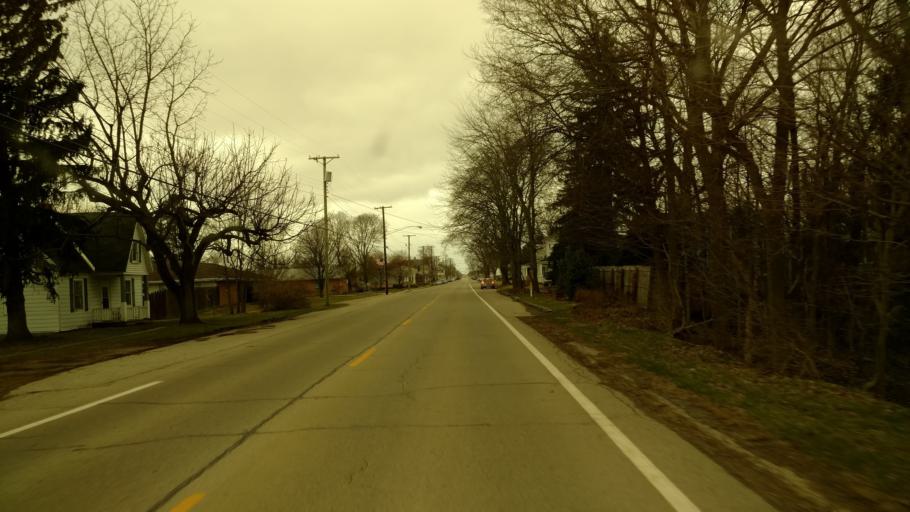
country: US
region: Ohio
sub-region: Fairfield County
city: Millersport
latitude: 39.9593
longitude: -82.5931
